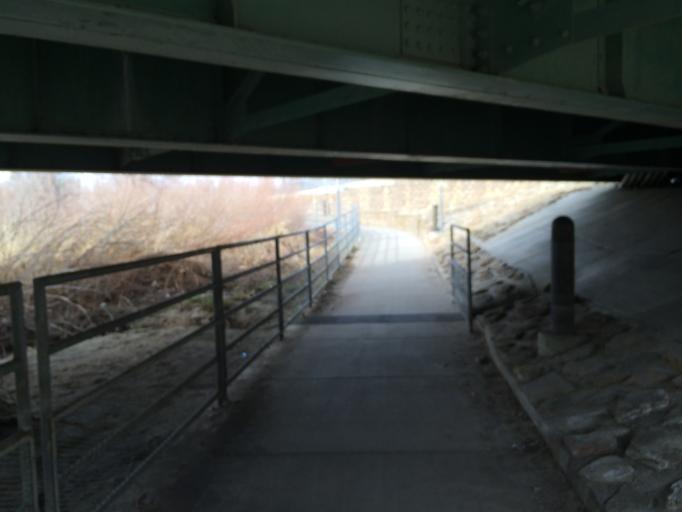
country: US
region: Wyoming
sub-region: Natrona County
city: Casper
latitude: 42.8571
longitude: -106.3273
